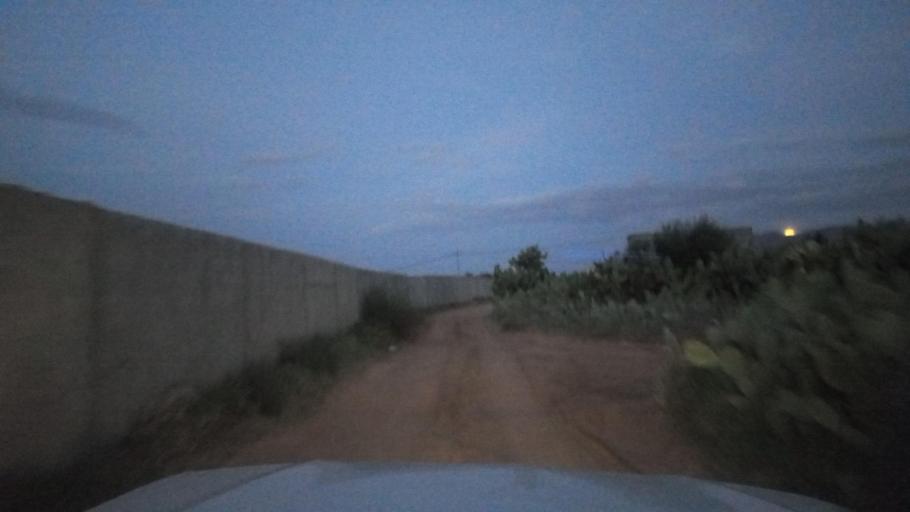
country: TN
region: Al Qasrayn
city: Sbiba
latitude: 35.4194
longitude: 9.1199
